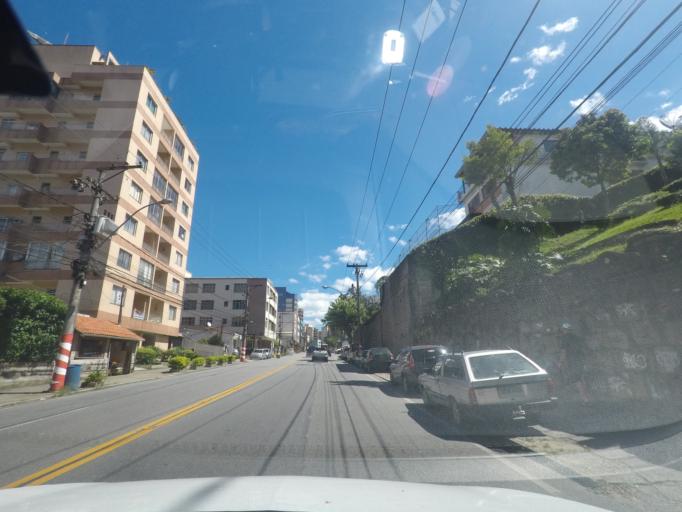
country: BR
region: Rio de Janeiro
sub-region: Teresopolis
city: Teresopolis
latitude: -22.4323
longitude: -42.9787
